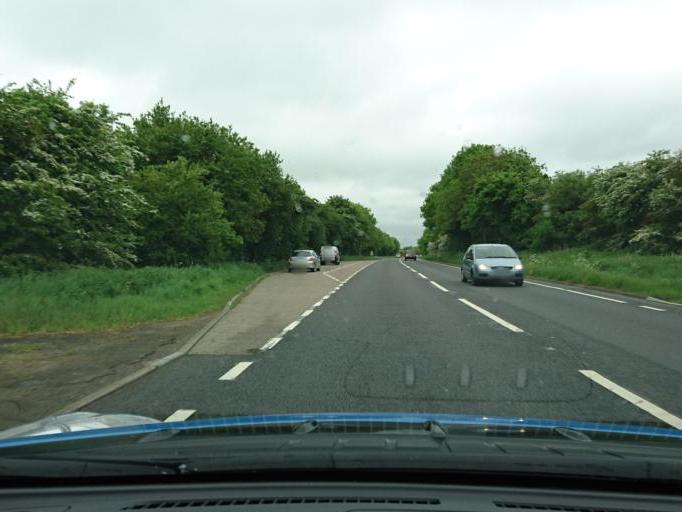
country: GB
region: England
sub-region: Oxfordshire
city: Shrivenham
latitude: 51.5972
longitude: -1.6693
